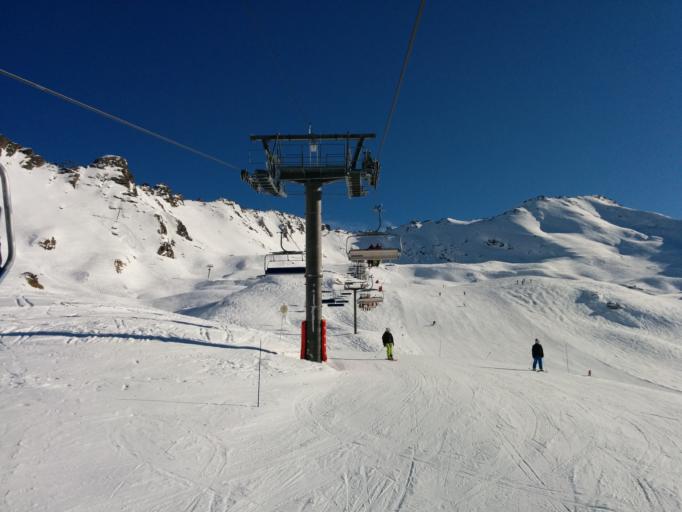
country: FR
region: Rhone-Alpes
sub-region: Departement de la Savoie
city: Val-d'Isere
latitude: 45.4239
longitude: 7.0077
